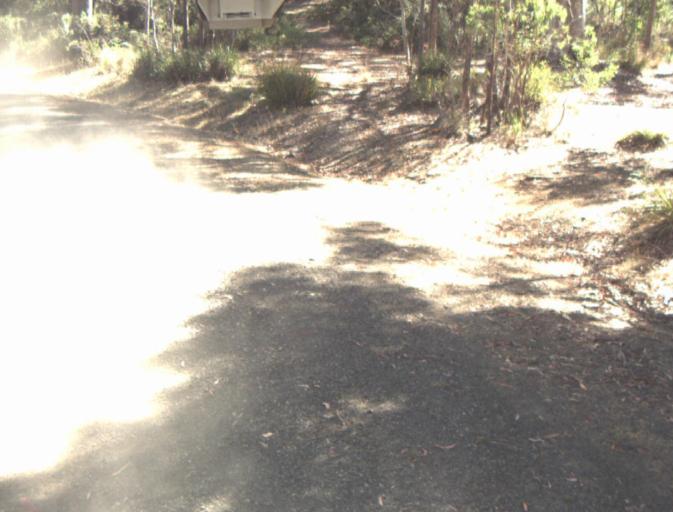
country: AU
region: Tasmania
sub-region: Launceston
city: Newstead
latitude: -41.3016
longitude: 147.3167
